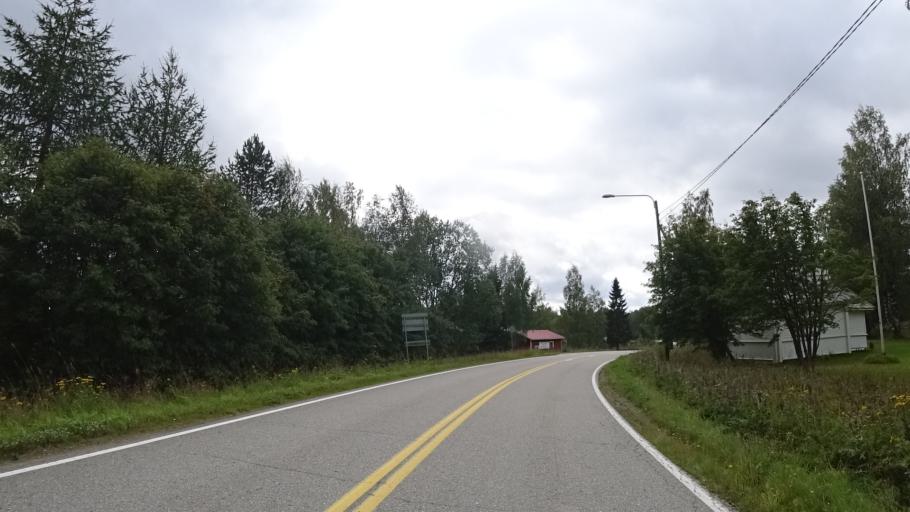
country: FI
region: North Karelia
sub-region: Joensuu
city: Ilomantsi
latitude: 62.9324
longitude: 31.2822
